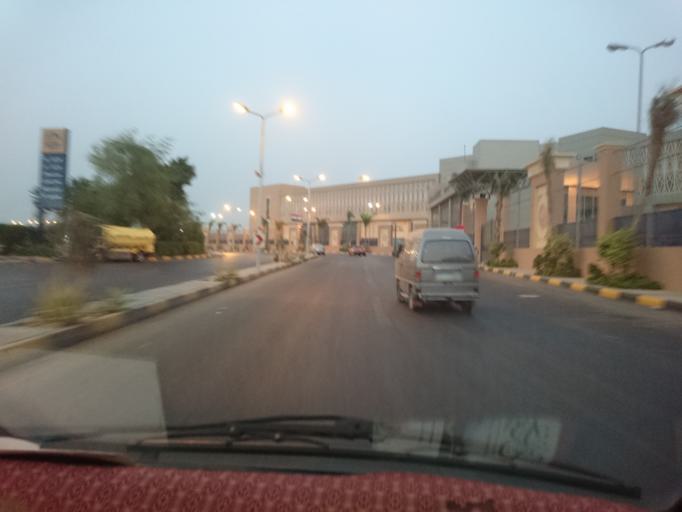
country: EG
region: Red Sea
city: Hurghada
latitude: 27.2318
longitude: 33.8449
